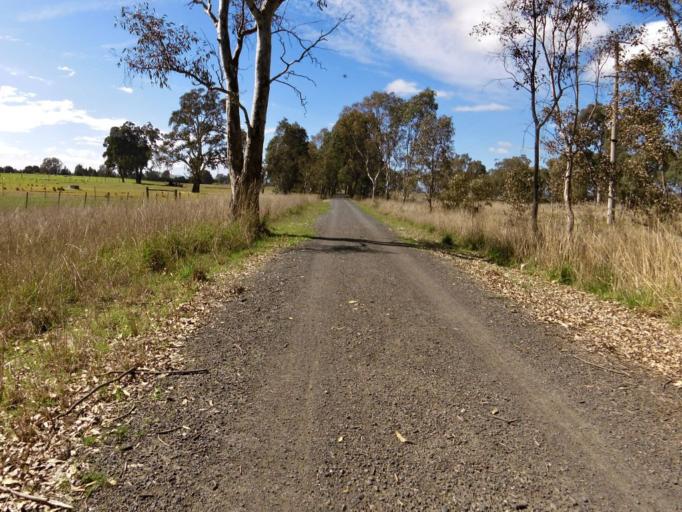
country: AU
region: Victoria
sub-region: Mansfield
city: Mansfield
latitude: -37.0479
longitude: 146.0618
